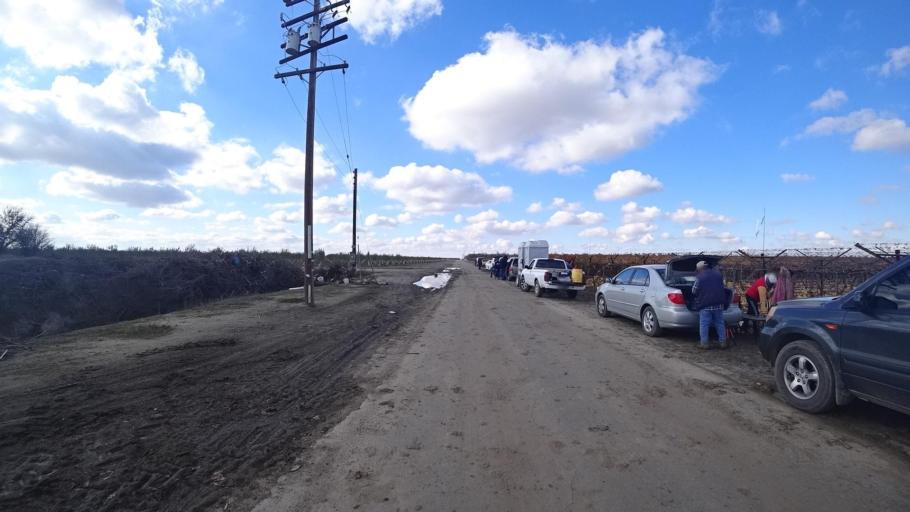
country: US
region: California
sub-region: Kern County
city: McFarland
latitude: 35.6670
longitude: -119.2491
